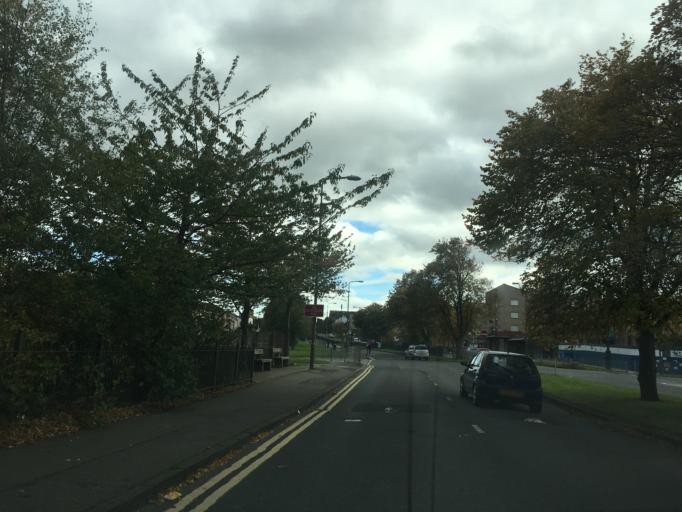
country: GB
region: Scotland
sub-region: Edinburgh
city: Edinburgh
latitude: 55.9730
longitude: -3.2529
